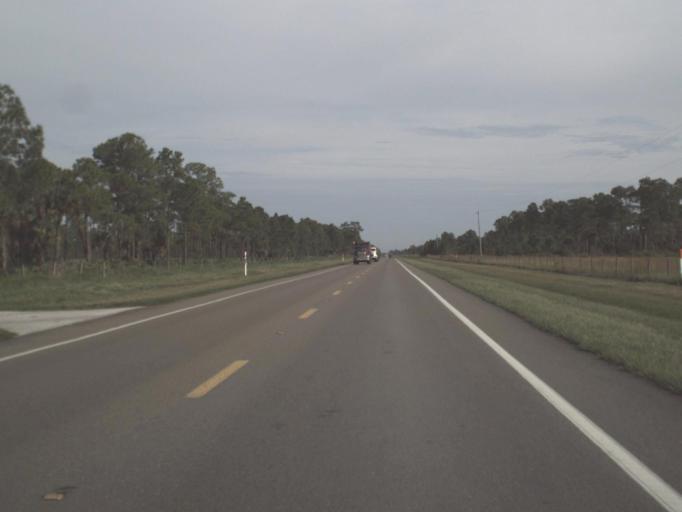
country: US
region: Florida
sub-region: Lee County
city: Olga
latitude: 26.8340
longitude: -81.7599
